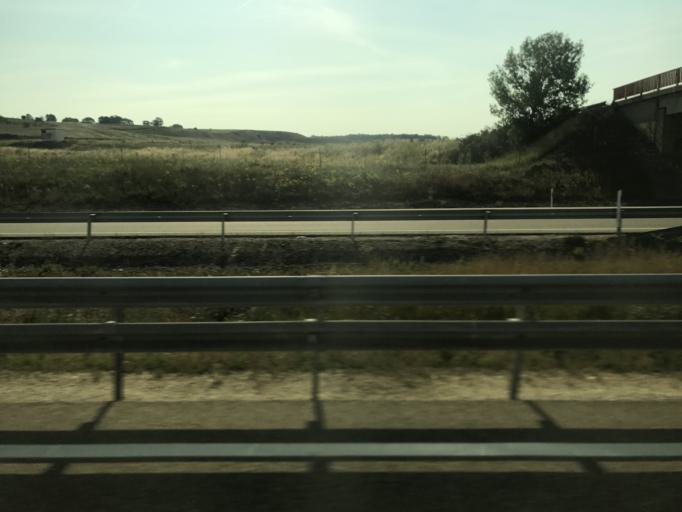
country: ES
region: Castille and Leon
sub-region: Provincia de Burgos
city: Cardenajimeno
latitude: 42.3507
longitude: -3.6033
